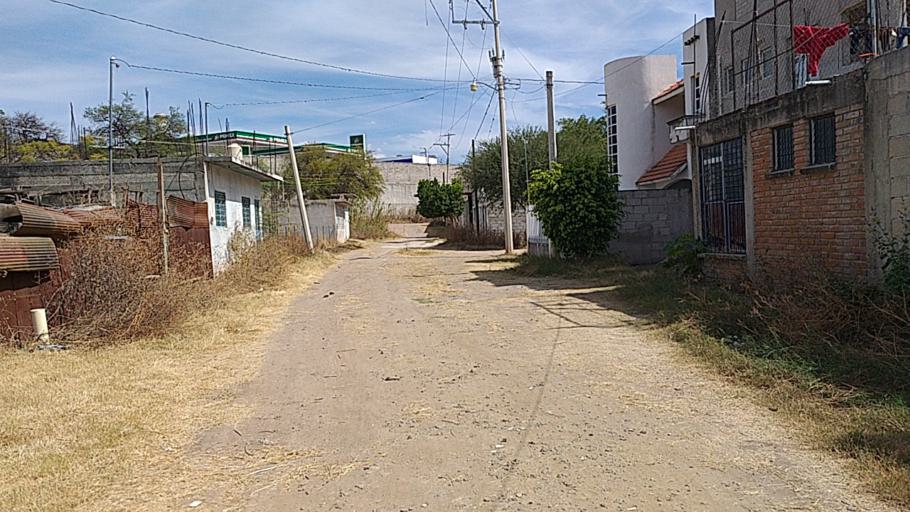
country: MX
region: Oaxaca
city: Ciudad de Huajuapam de Leon
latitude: 17.8129
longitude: -97.7641
